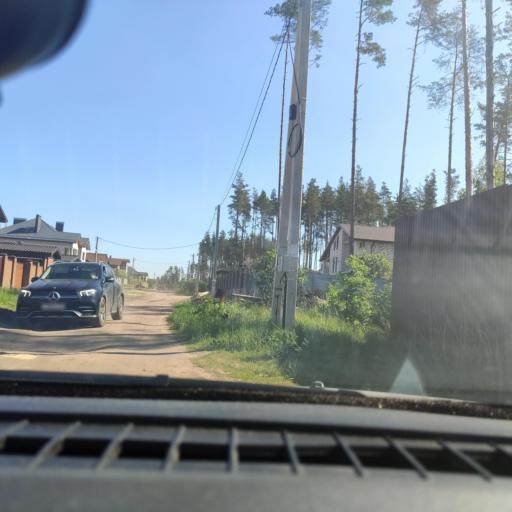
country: RU
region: Voronezj
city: Podgornoye
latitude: 51.7796
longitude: 39.1457
